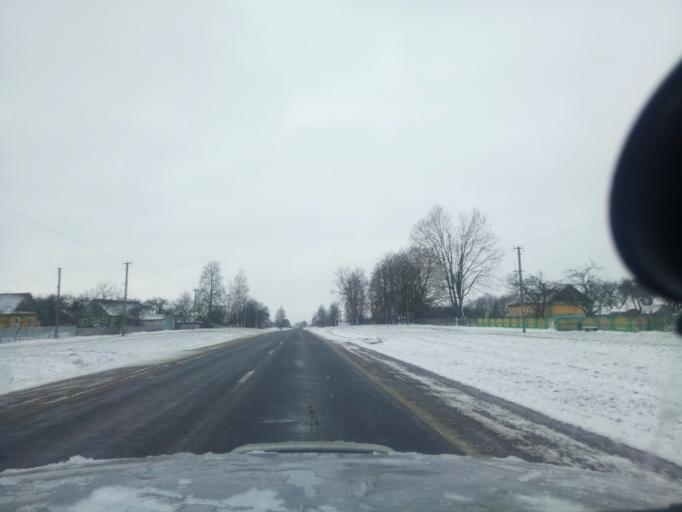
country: BY
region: Minsk
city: Klyetsk
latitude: 53.1200
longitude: 26.6651
